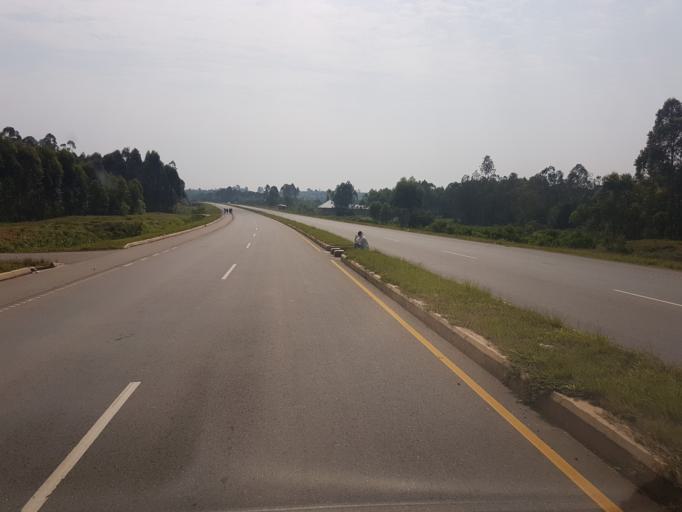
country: UG
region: Western Region
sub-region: Mbarara District
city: Bwizibwera
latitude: -0.6368
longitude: 30.5955
